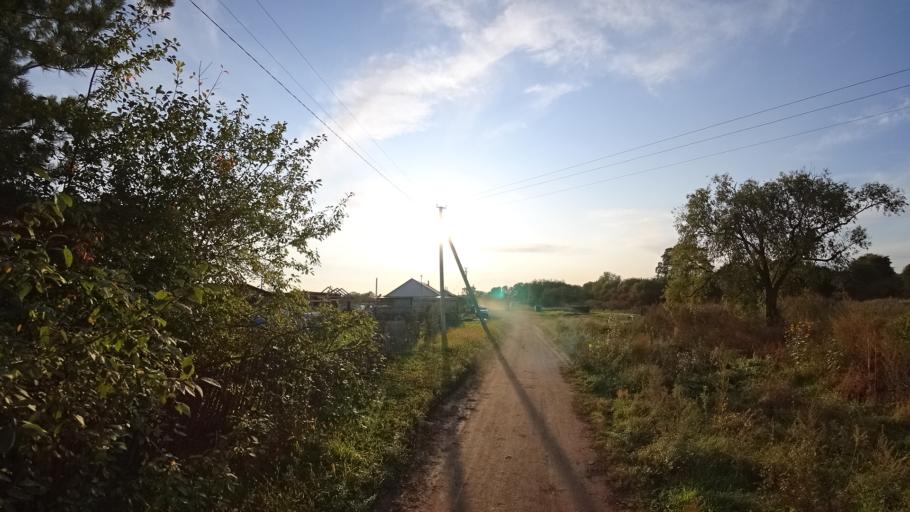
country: RU
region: Amur
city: Arkhara
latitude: 49.3585
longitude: 130.1211
